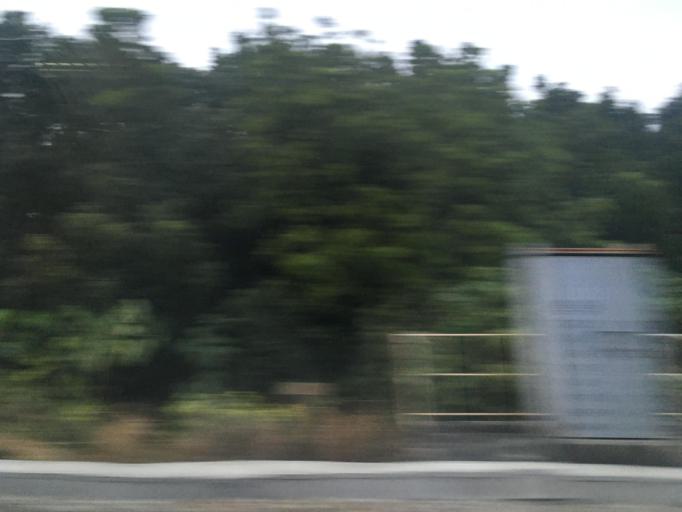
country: TW
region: Taiwan
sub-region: Pingtung
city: Pingtung
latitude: 22.6619
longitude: 120.4479
